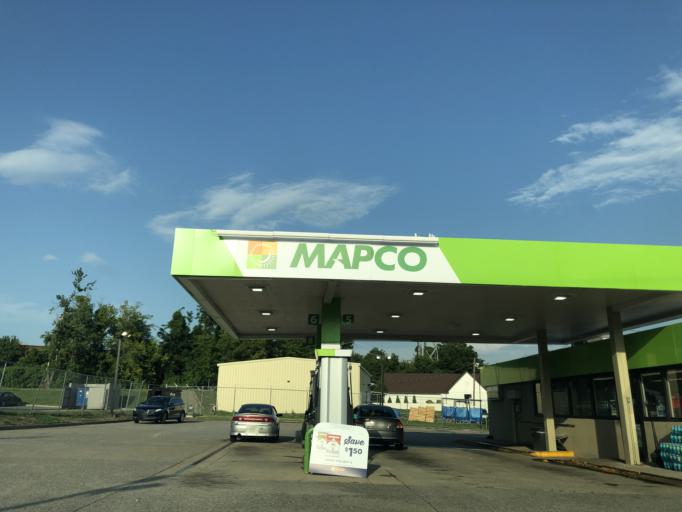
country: US
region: Tennessee
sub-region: Davidson County
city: Lakewood
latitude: 36.1512
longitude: -86.6664
